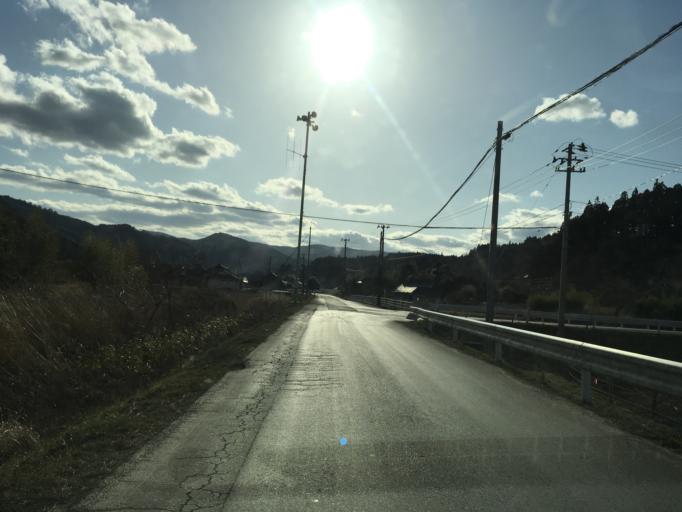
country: JP
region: Iwate
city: Ofunato
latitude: 39.0290
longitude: 141.5972
